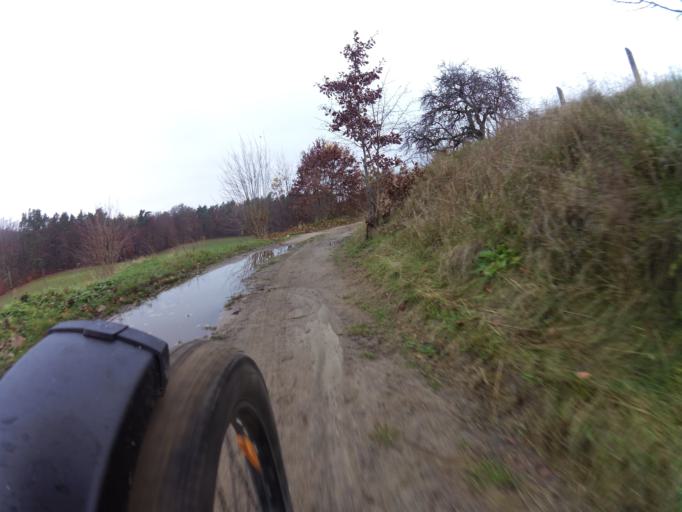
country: PL
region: Pomeranian Voivodeship
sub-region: Powiat pucki
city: Krokowa
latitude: 54.7222
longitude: 18.1338
